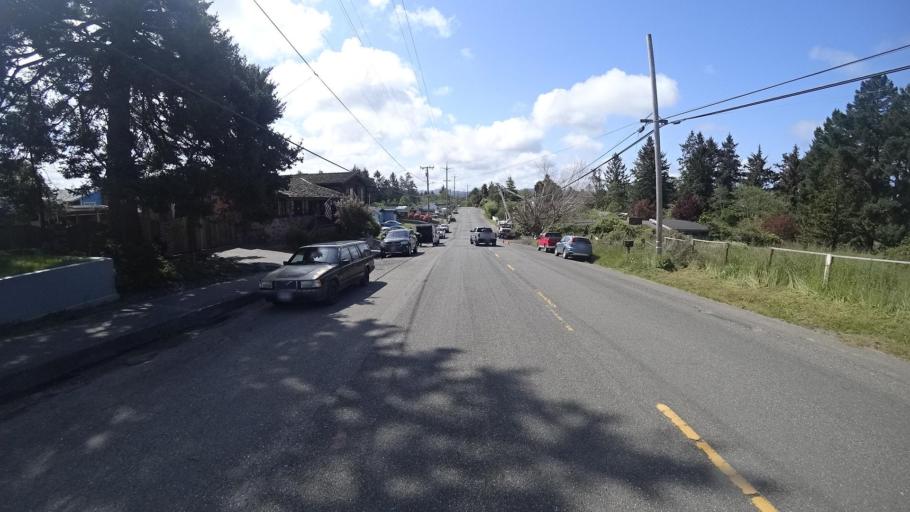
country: US
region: California
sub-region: Humboldt County
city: Bayview
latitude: 40.7629
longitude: -124.1778
